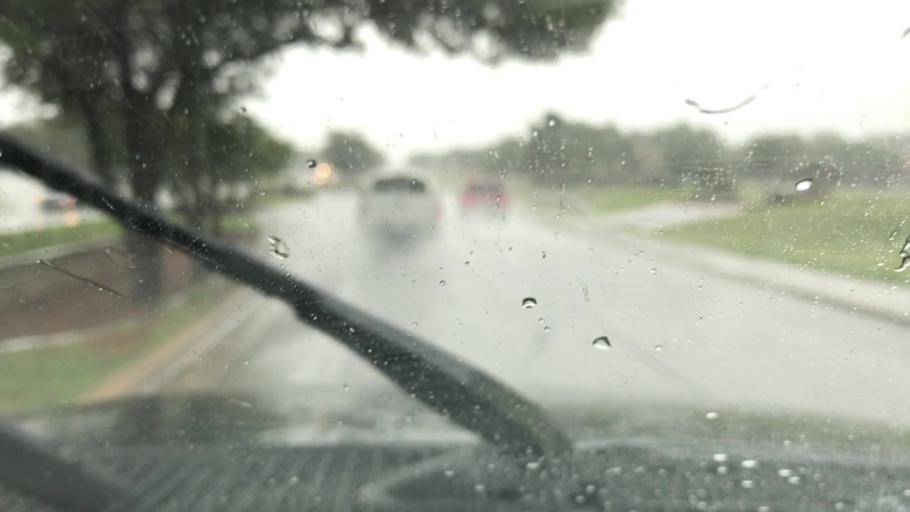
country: US
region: Texas
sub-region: Williamson County
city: Leander
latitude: 30.5362
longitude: -97.8609
